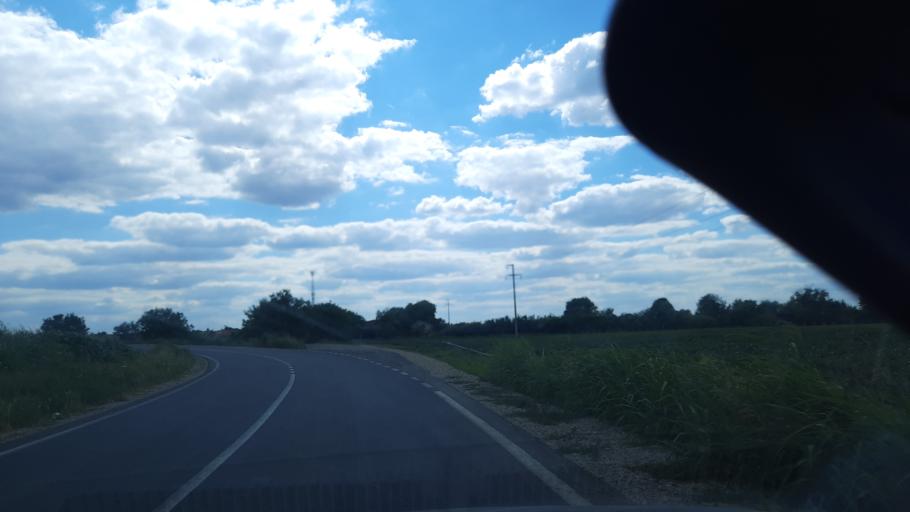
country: RS
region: Autonomna Pokrajina Vojvodina
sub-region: Sremski Okrug
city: Pecinci
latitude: 44.9194
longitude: 19.9745
